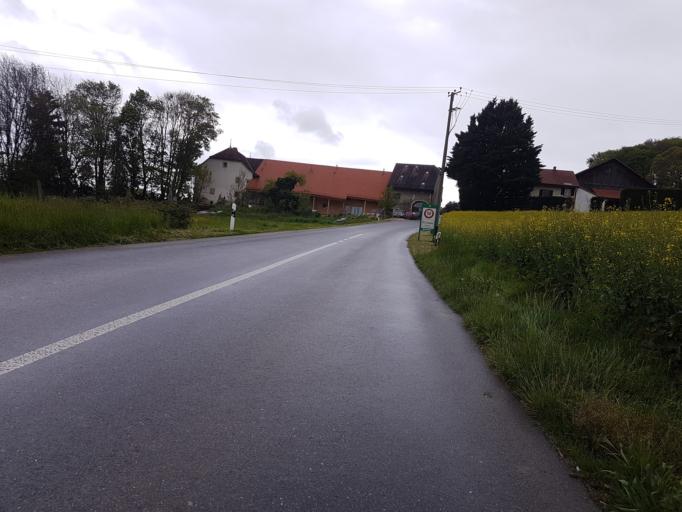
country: CH
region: Vaud
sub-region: Gros-de-Vaud District
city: Penthalaz
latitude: 46.5960
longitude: 6.5269
